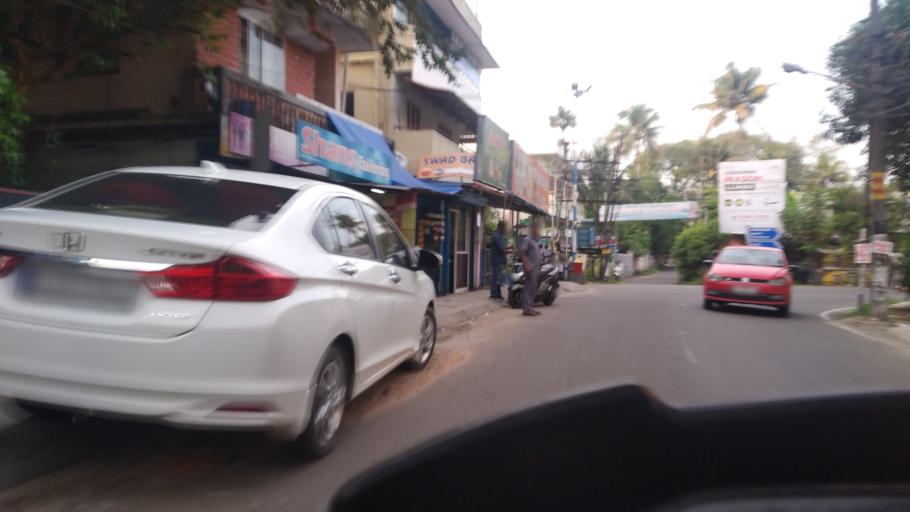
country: IN
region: Kerala
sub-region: Ernakulam
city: Elur
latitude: 10.0178
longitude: 76.2843
